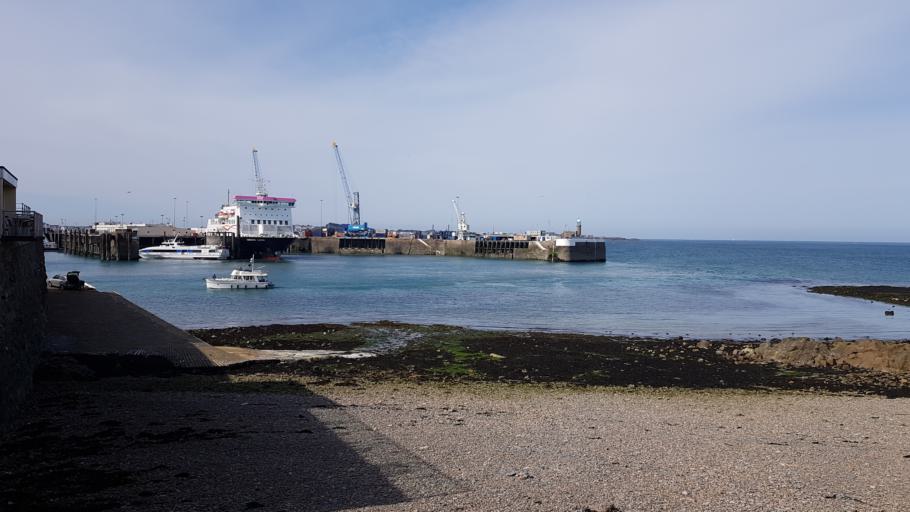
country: GG
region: St Peter Port
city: Saint Peter Port
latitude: 49.4534
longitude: -2.5284
